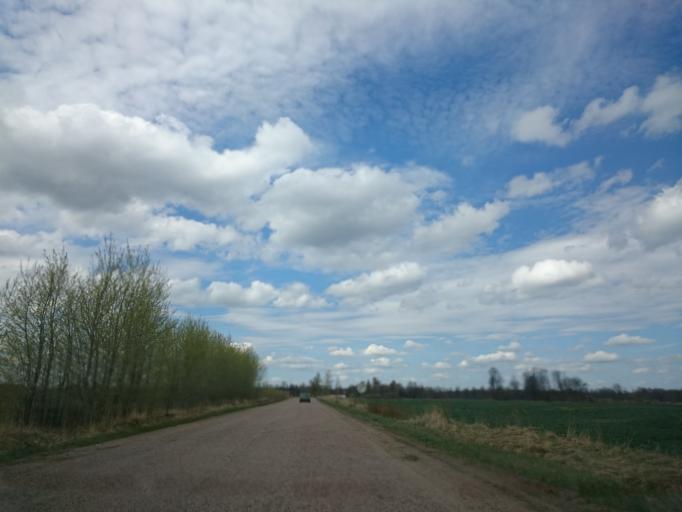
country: LV
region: Talsu Rajons
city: Sabile
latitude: 56.9583
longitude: 22.6259
